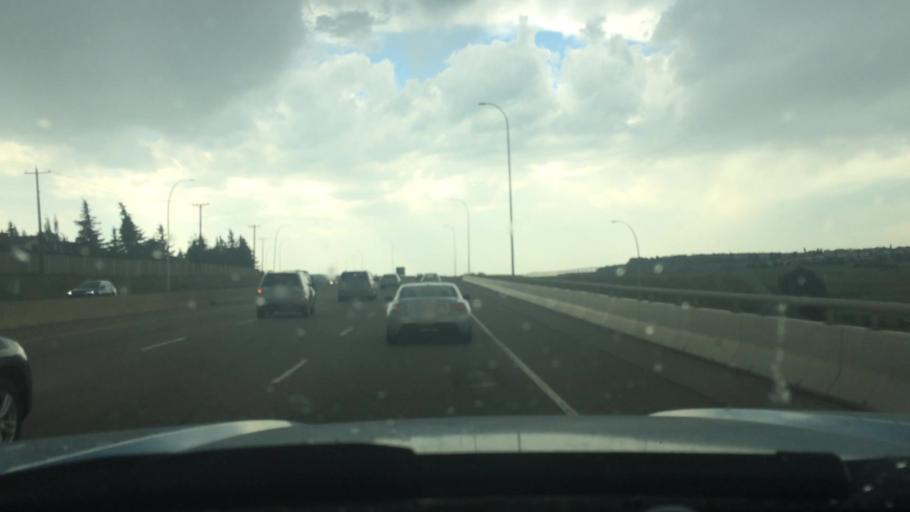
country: CA
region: Alberta
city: Calgary
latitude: 51.1354
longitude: -114.0734
